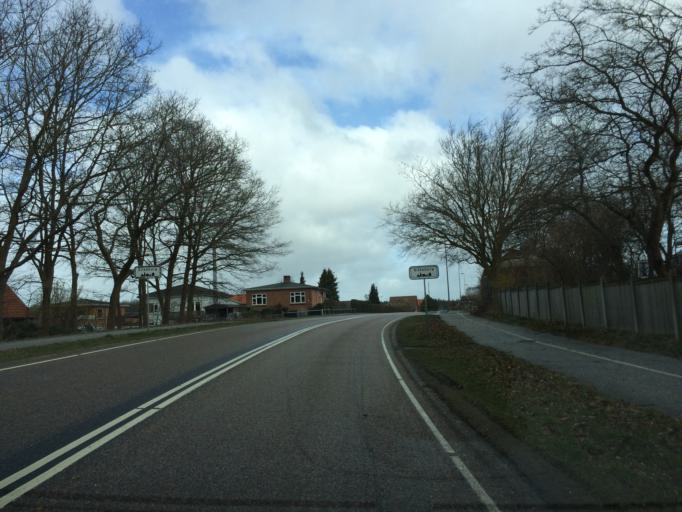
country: DK
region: Central Jutland
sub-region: Silkeborg Kommune
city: Silkeborg
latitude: 56.1560
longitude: 9.5329
